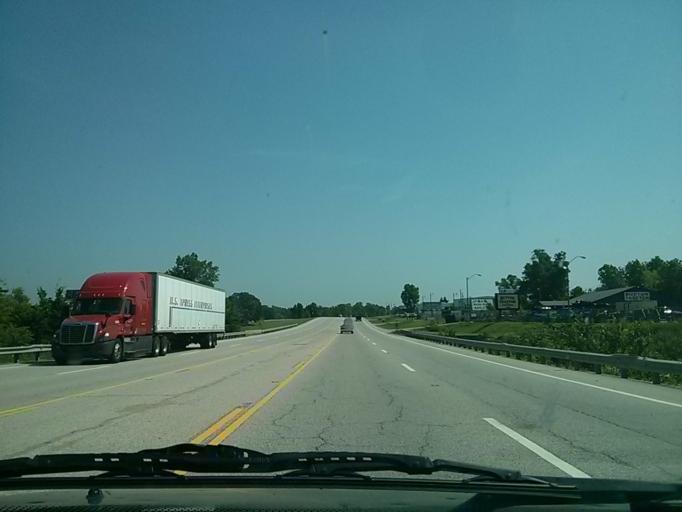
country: US
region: Oklahoma
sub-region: Tulsa County
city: Oakhurst
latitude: 36.0617
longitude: -96.0695
